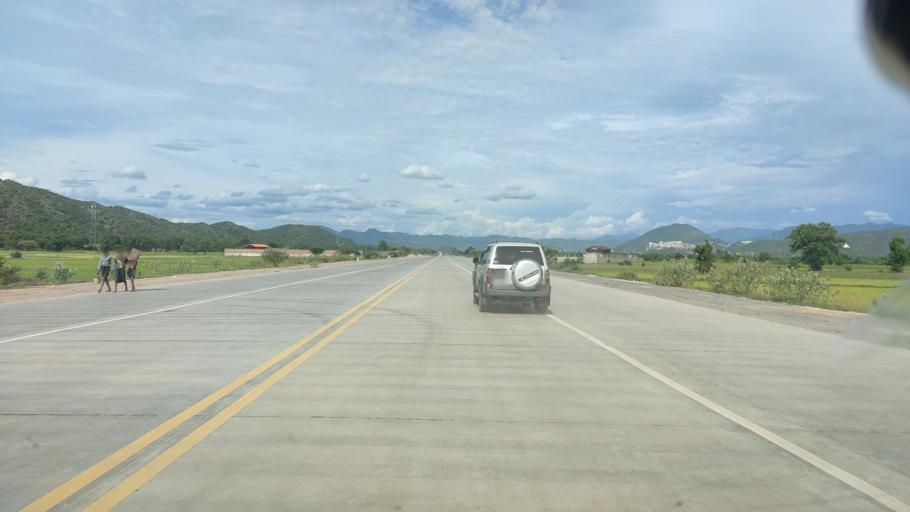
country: MM
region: Mandalay
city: Kyaukse
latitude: 21.5935
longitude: 96.1553
